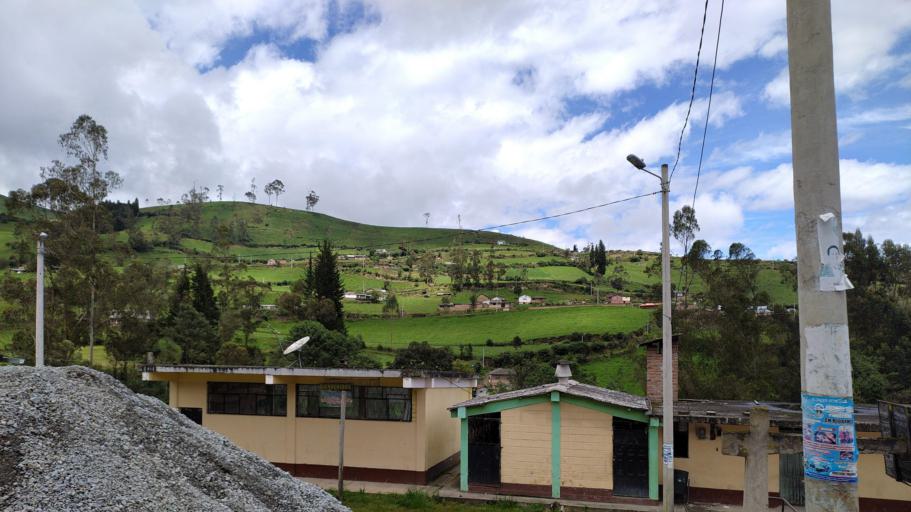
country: EC
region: Chimborazo
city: Riobamba
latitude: -1.6733
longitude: -78.5673
